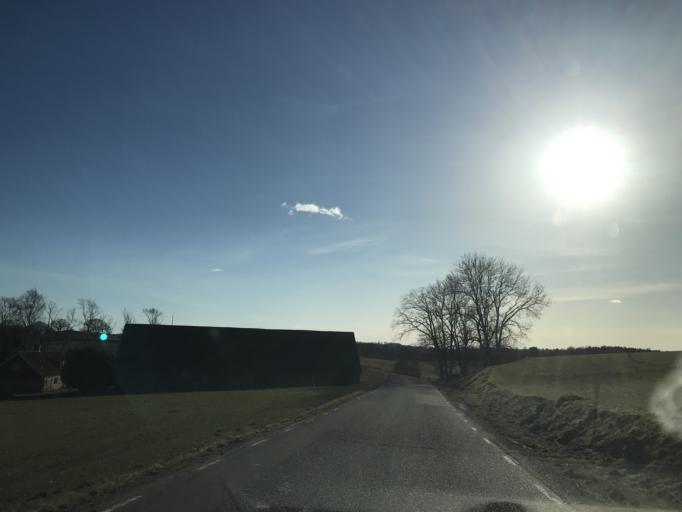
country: SE
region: Skane
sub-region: Ystads Kommun
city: Ystad
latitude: 55.5453
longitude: 13.7909
